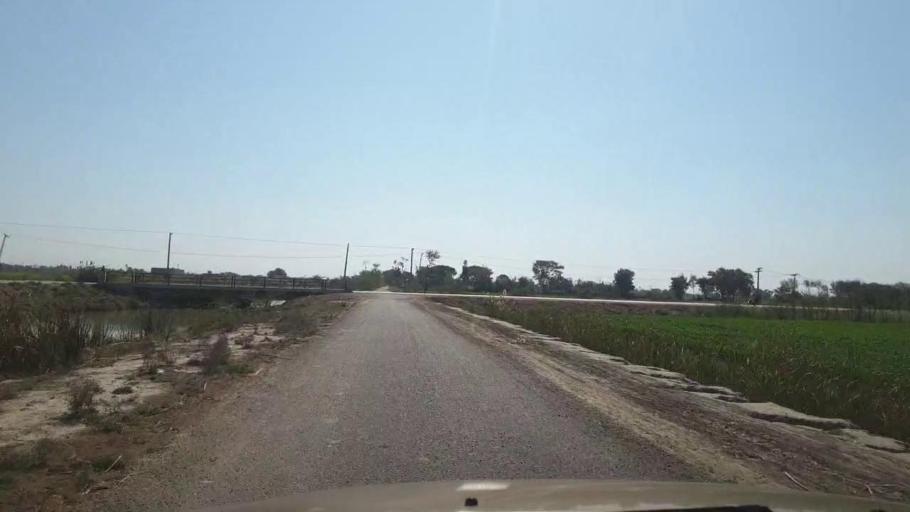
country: PK
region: Sindh
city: Mirpur Khas
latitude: 25.5678
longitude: 69.0622
